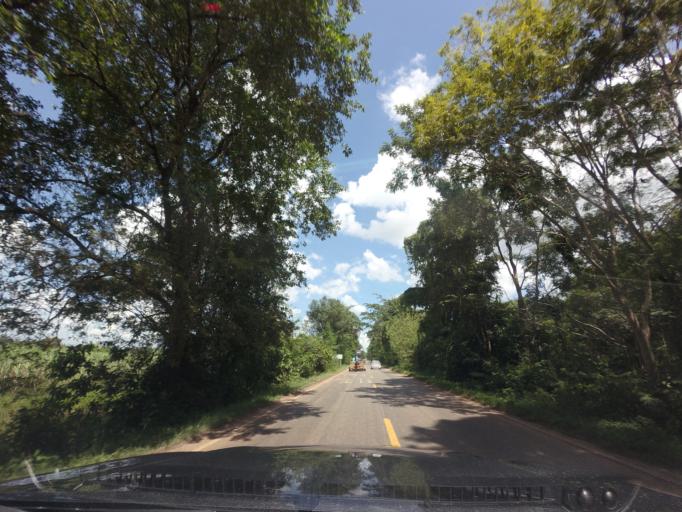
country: TH
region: Changwat Udon Thani
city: Ban Dung
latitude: 17.6694
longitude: 103.1675
